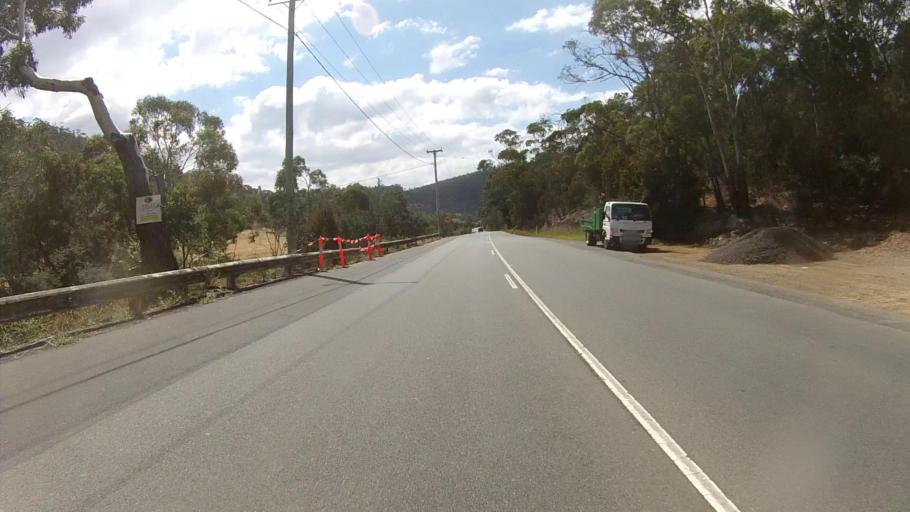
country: AU
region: Tasmania
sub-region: Clarence
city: Cambridge
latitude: -42.8446
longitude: 147.4200
